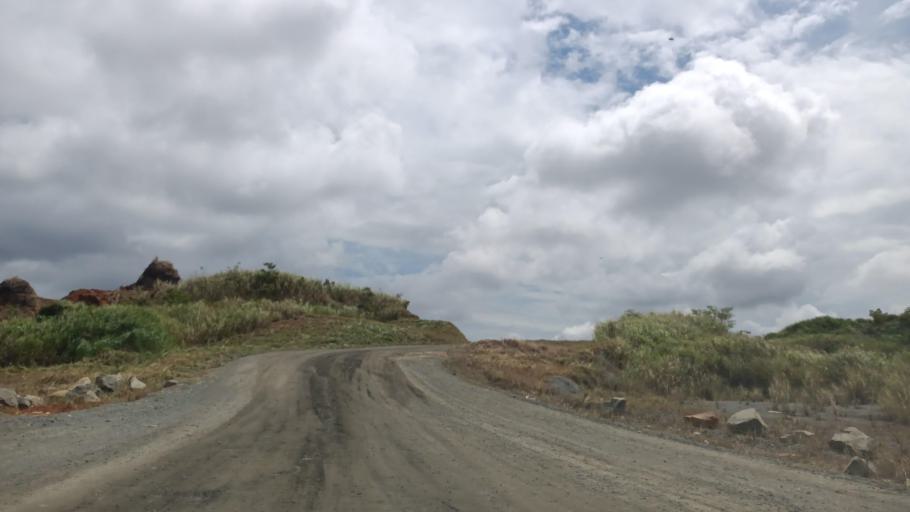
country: PA
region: Panama
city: Las Cumbres
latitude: 9.1058
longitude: -79.4998
